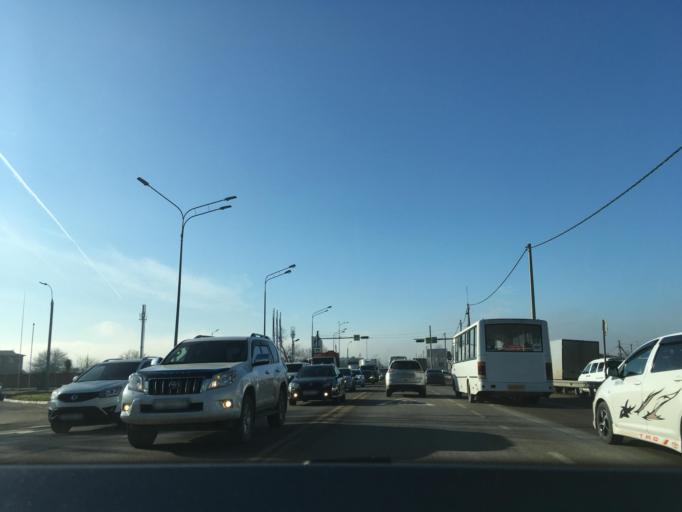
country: RU
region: Krasnodarskiy
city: Krasnodar
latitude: 45.1281
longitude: 39.0138
